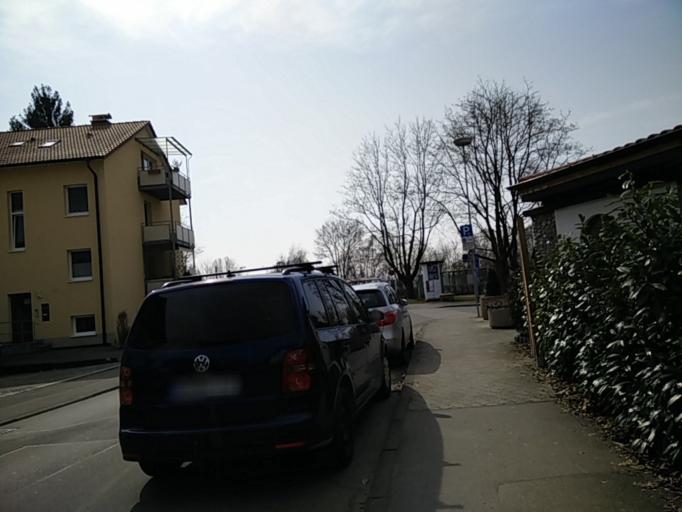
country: DE
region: Baden-Wuerttemberg
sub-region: Freiburg Region
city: Radolfzell am Bodensee
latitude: 47.7400
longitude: 9.0029
